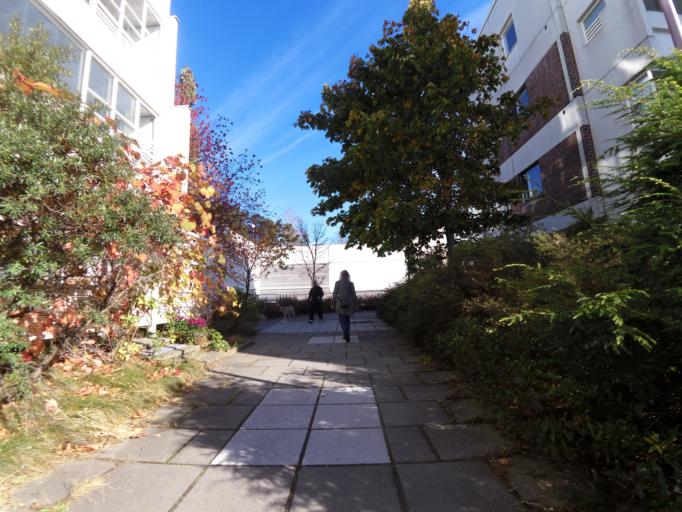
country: FI
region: Uusimaa
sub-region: Helsinki
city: Espoo
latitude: 60.1519
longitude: 24.6282
